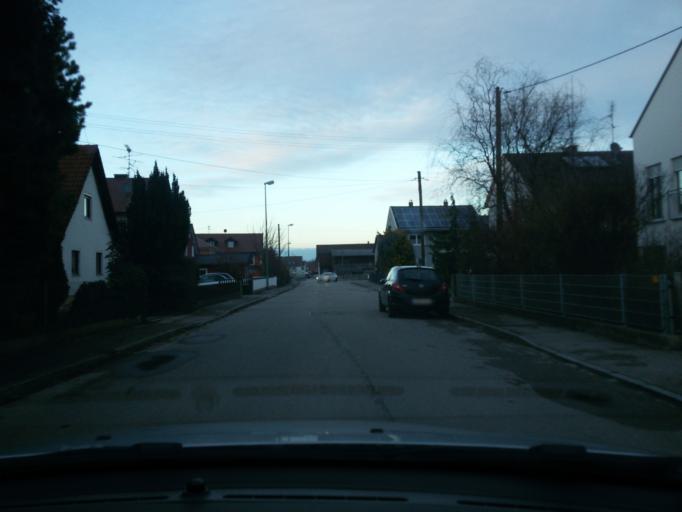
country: DE
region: Bavaria
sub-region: Swabia
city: Schwabmunchen
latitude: 48.1739
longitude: 10.7496
